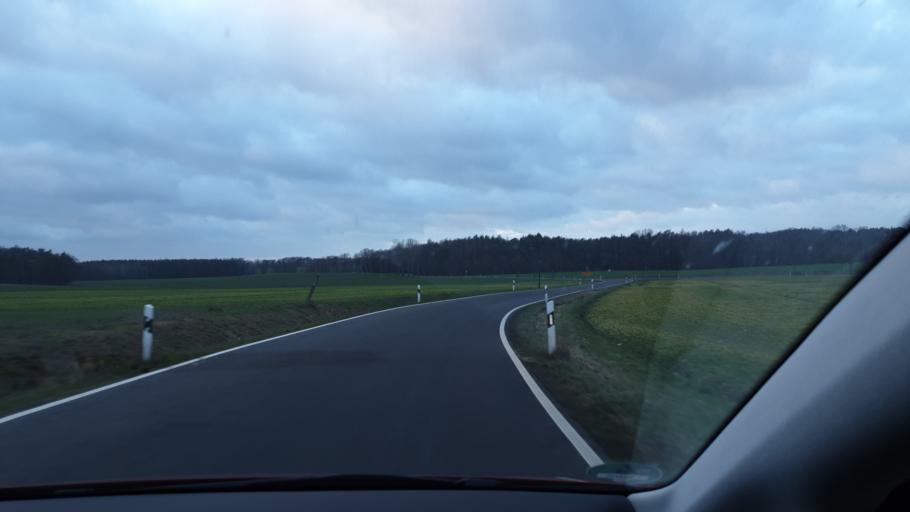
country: DE
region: Saxony
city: Falkenhain
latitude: 51.4525
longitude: 12.8586
